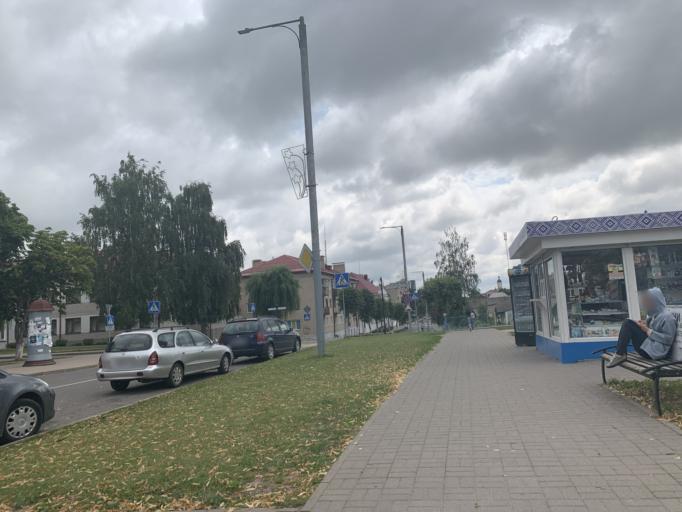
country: BY
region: Minsk
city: Nyasvizh
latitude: 53.2224
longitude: 26.6707
